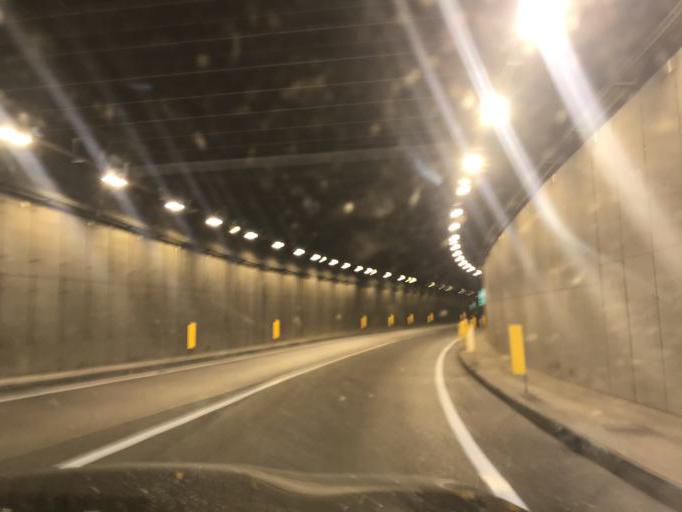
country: IT
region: Sardinia
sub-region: Provincia di Olbia-Tempio
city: Olbia
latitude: 40.9253
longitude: 9.5070
